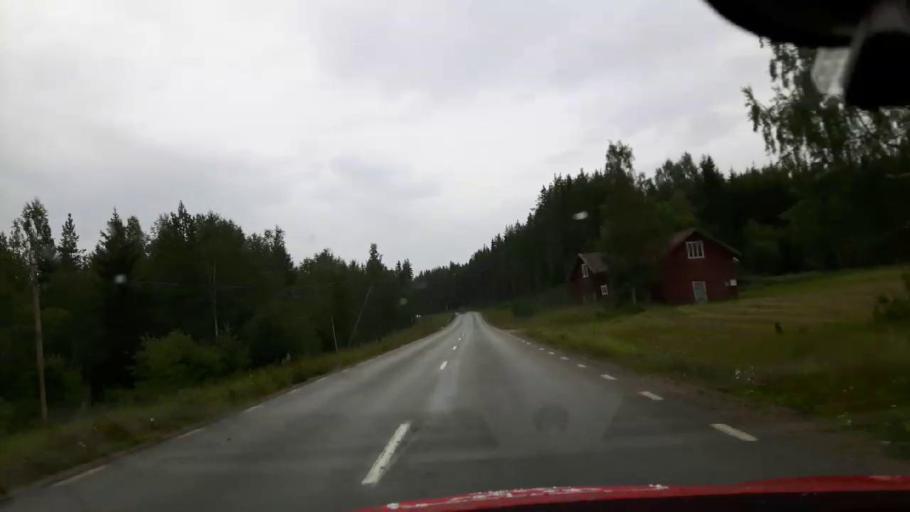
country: SE
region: Jaemtland
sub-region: OEstersunds Kommun
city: Brunflo
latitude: 62.8367
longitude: 15.0072
